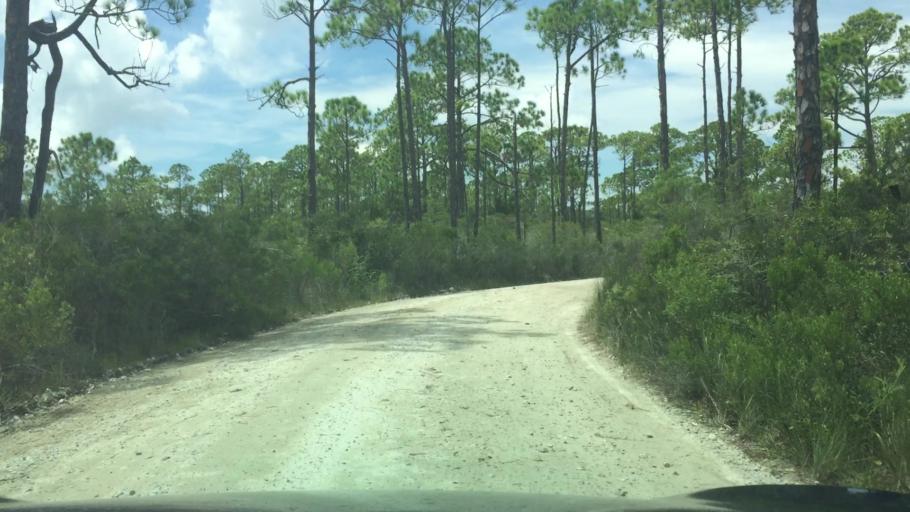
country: US
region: Florida
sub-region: Bay County
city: Mexico Beach
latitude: 29.9609
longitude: -85.4558
